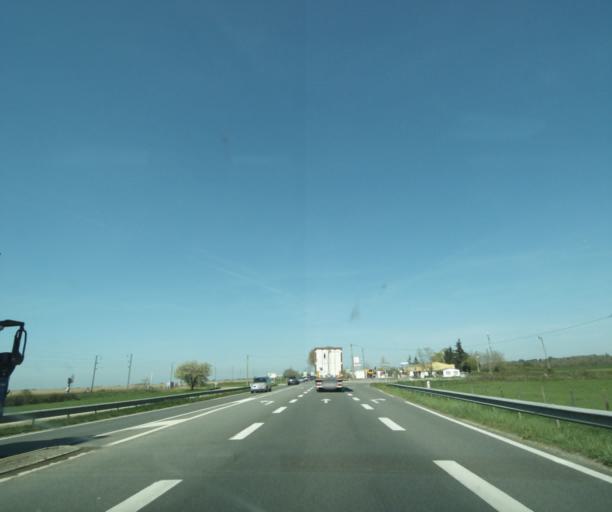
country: FR
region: Bourgogne
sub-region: Departement de la Nievre
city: Chantenay-Saint-Imbert
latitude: 46.7024
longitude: 3.2026
